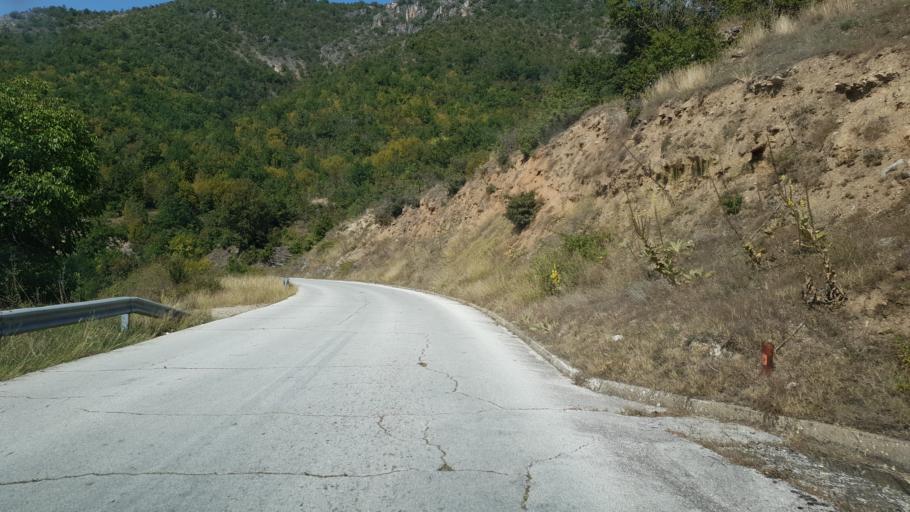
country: MK
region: Makedonski Brod
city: Samokov
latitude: 41.6701
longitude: 21.2419
